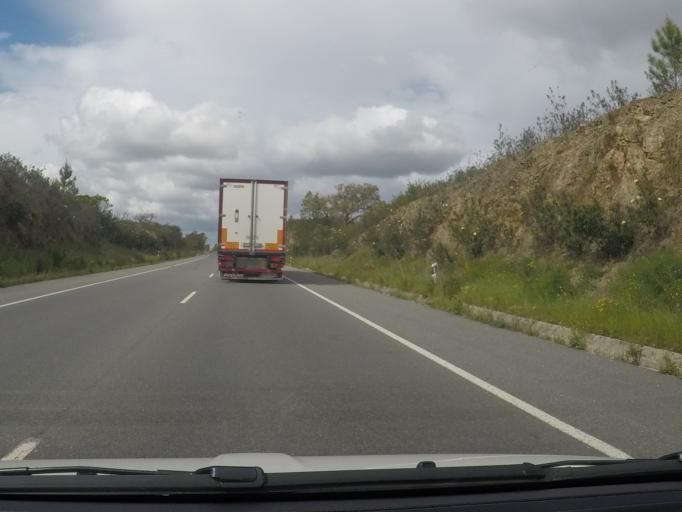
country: PT
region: Setubal
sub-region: Grandola
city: Grandola
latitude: 38.1478
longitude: -8.6499
